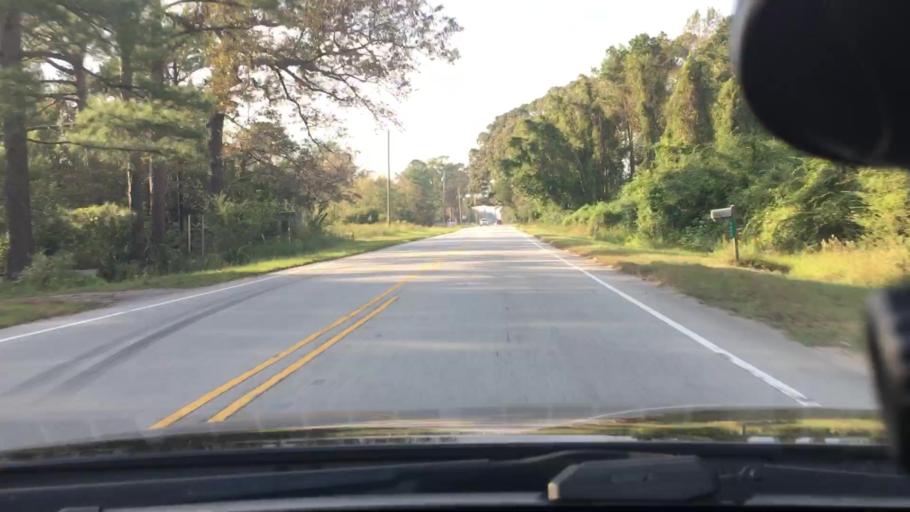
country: US
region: North Carolina
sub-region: Craven County
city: Vanceboro
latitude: 35.2383
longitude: -77.0765
